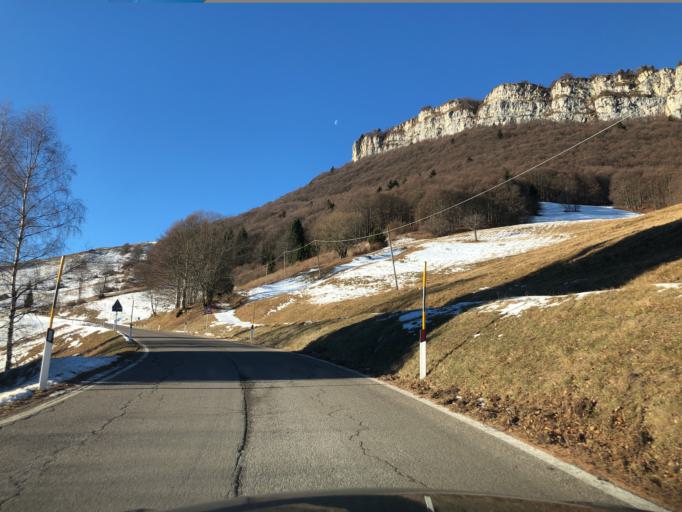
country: IT
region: Trentino-Alto Adige
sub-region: Provincia di Trento
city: Brentonico
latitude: 45.7890
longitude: 10.9170
